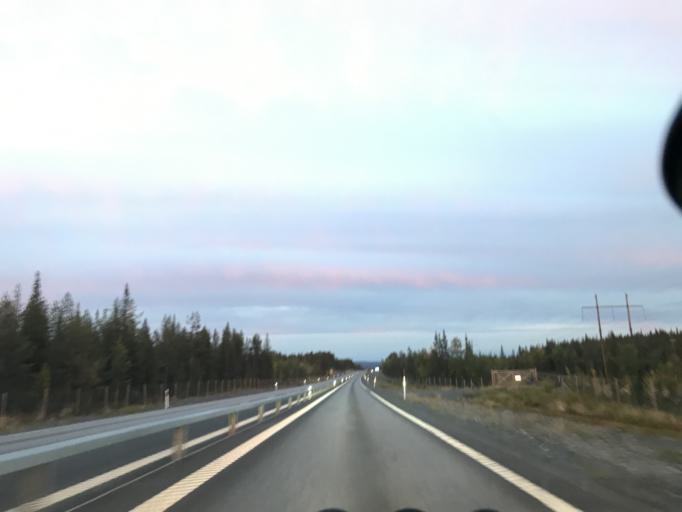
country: SE
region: Norrbotten
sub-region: Gallivare Kommun
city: Malmberget
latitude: 67.6864
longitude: 20.8538
